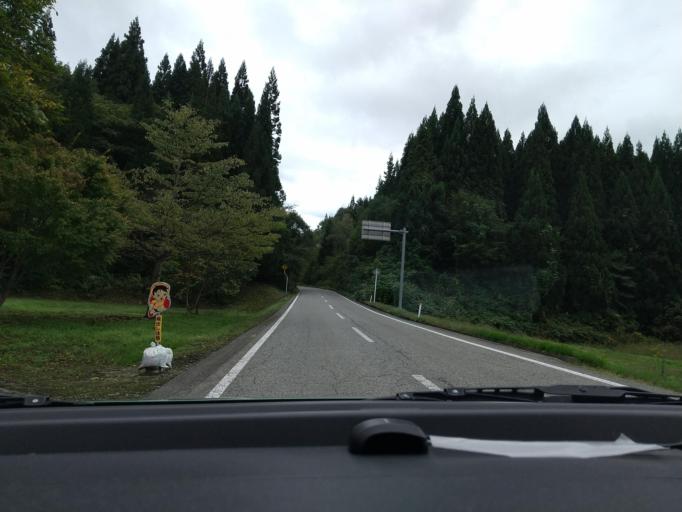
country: JP
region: Akita
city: Kakunodatemachi
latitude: 39.5529
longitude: 140.6330
